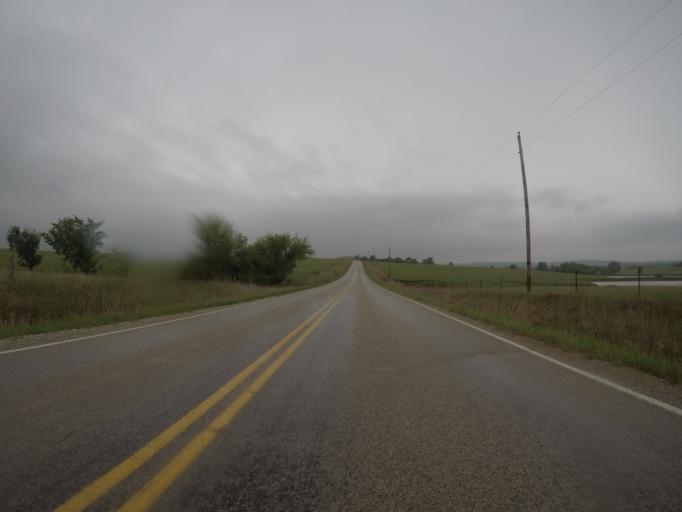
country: US
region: Kansas
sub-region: Pottawatomie County
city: Westmoreland
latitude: 39.4238
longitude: -96.1839
